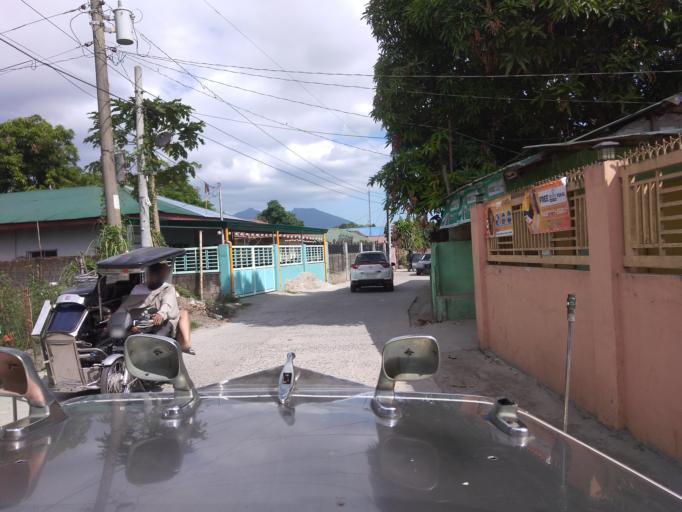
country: PH
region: Central Luzon
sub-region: Province of Pampanga
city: Pandacaqui
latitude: 15.1841
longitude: 120.6449
